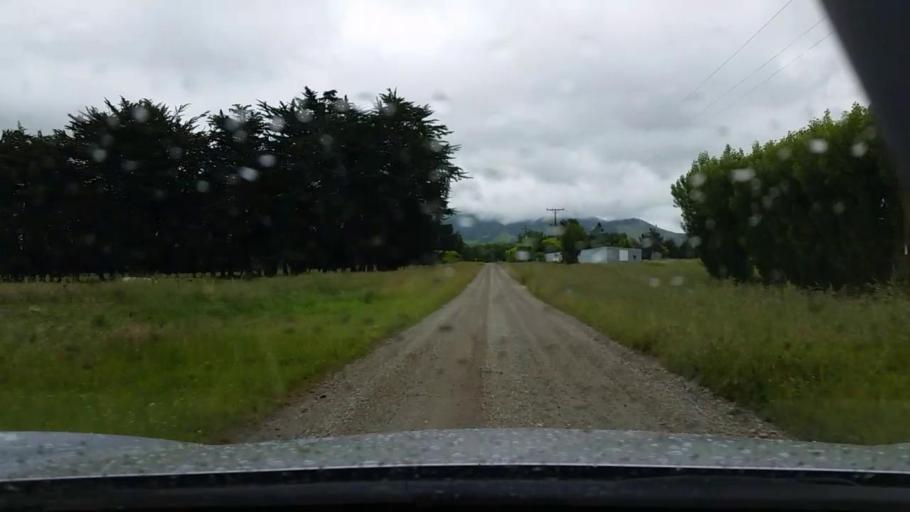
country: NZ
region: Southland
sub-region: Gore District
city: Gore
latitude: -46.0712
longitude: 168.9566
